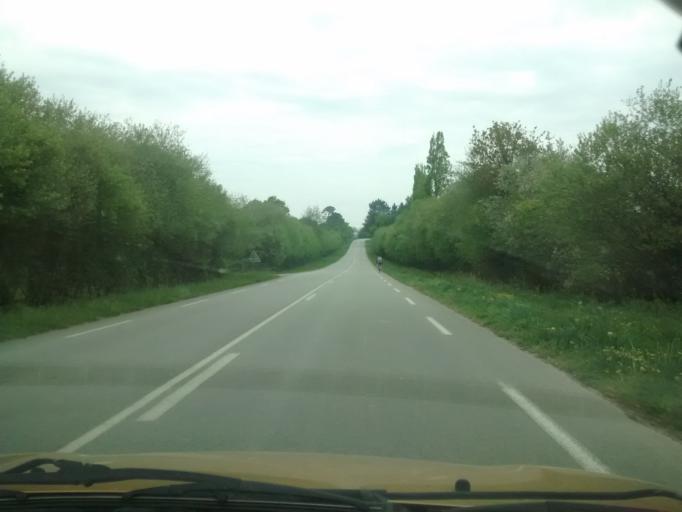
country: FR
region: Brittany
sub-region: Departement du Morbihan
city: Berric
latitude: 47.6199
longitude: -2.5354
